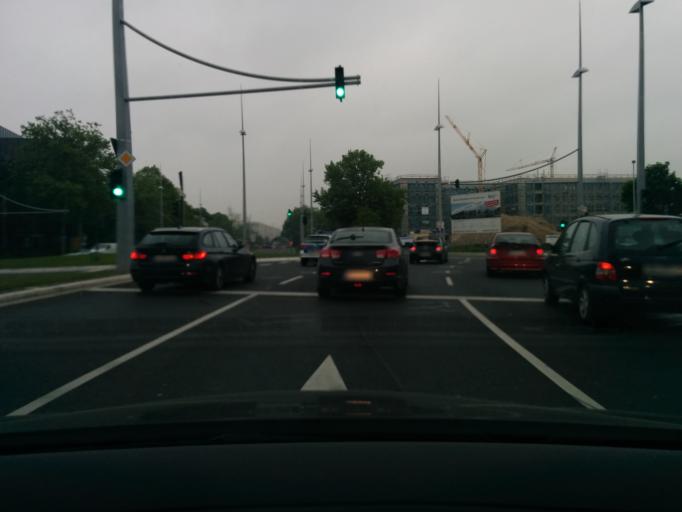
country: DE
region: North Rhine-Westphalia
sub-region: Regierungsbezirk Koln
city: Bonn
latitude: 50.7138
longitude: 7.1238
